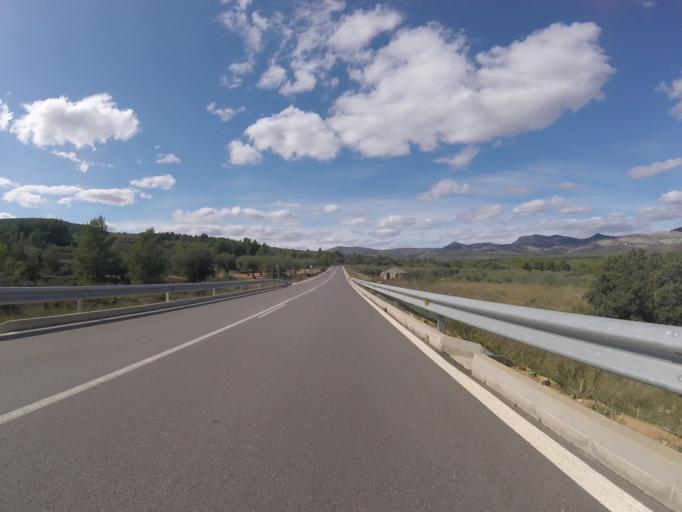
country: ES
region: Valencia
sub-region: Provincia de Castello
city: Chert/Xert
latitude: 40.4381
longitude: 0.1162
